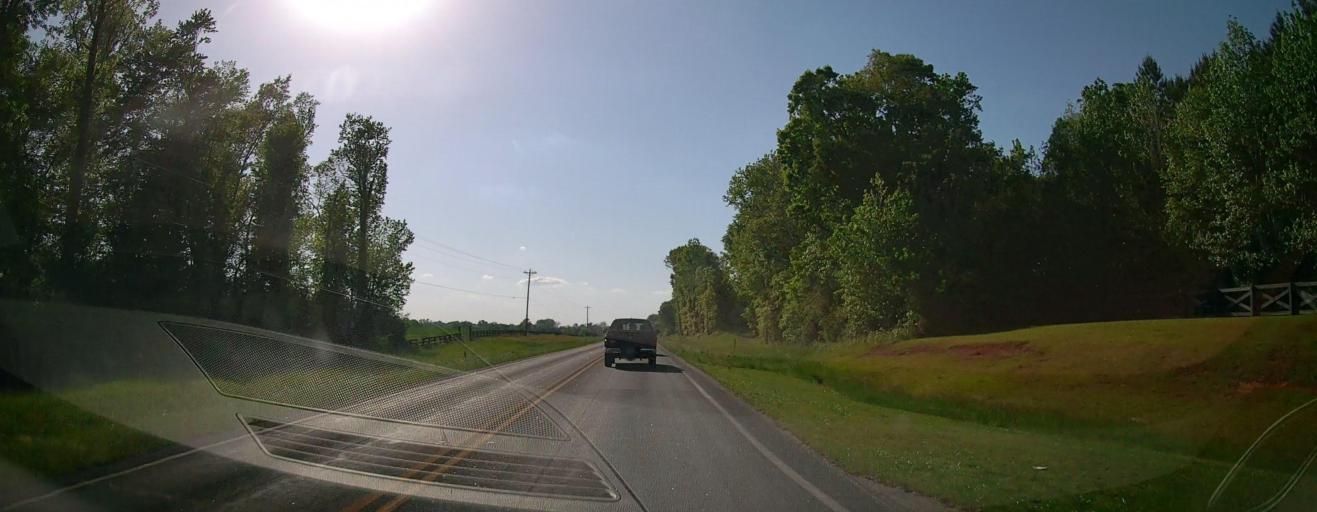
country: US
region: Georgia
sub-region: Morgan County
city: Madison
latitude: 33.5892
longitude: -83.5185
